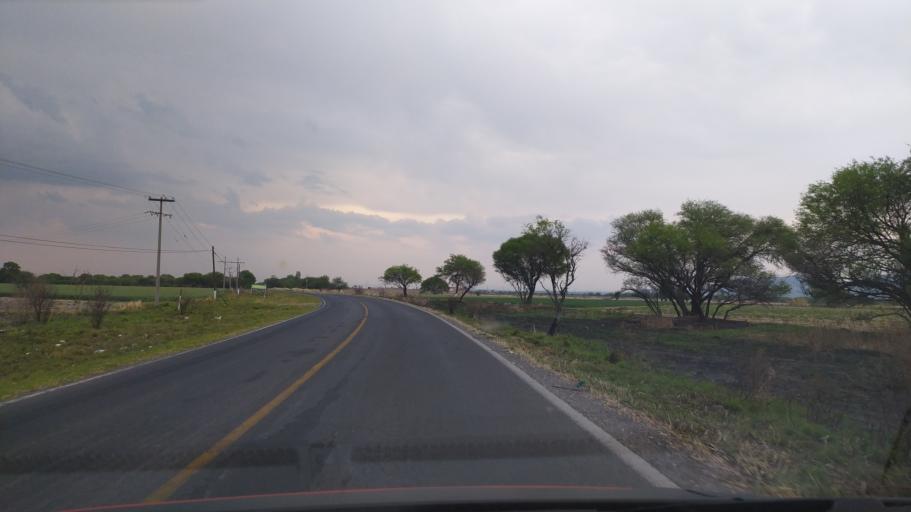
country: MX
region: Guanajuato
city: Ciudad Manuel Doblado
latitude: 20.7611
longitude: -101.9163
